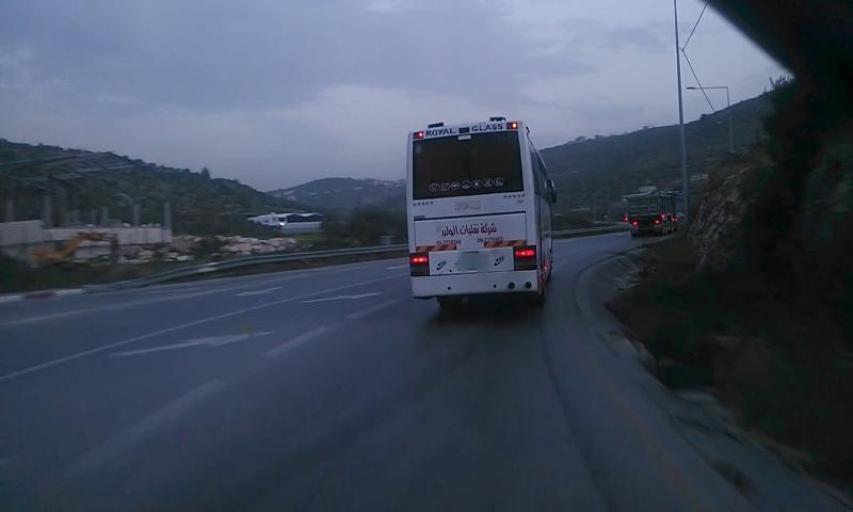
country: PS
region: West Bank
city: Kafr al Labad
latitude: 32.3163
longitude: 35.0919
